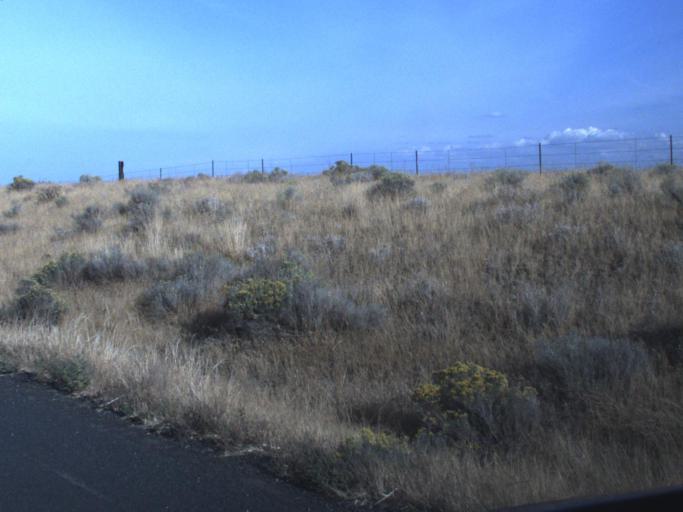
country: US
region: Oregon
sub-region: Morrow County
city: Boardman
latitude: 45.9135
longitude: -119.6624
